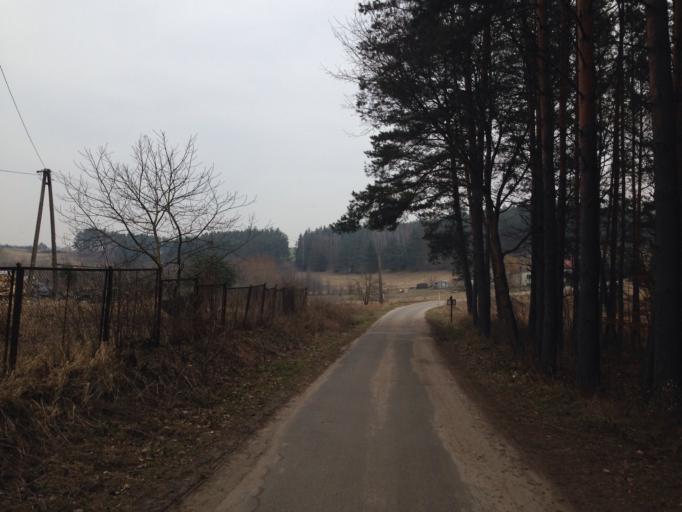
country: PL
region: Pomeranian Voivodeship
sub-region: Powiat kwidzynski
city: Sadlinki
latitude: 53.7232
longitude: 18.8105
